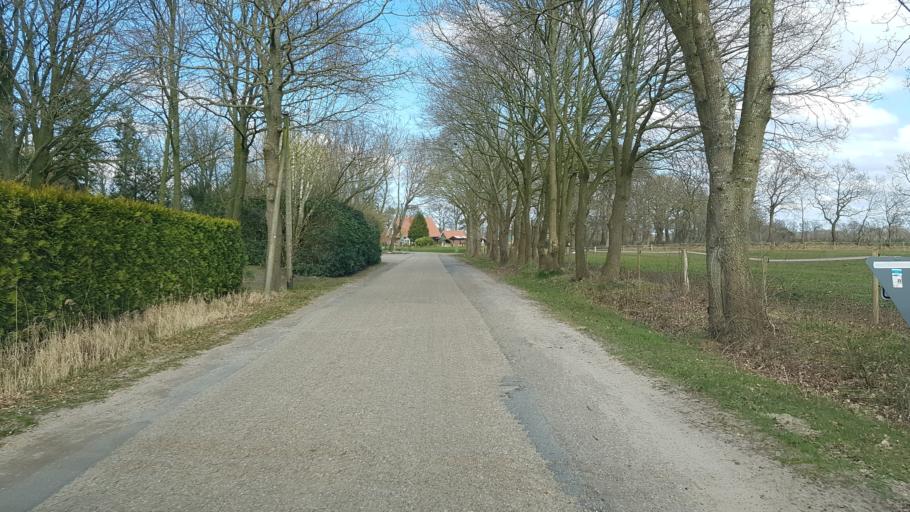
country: DE
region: Lower Saxony
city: Edewecht
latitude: 53.1611
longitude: 7.9366
